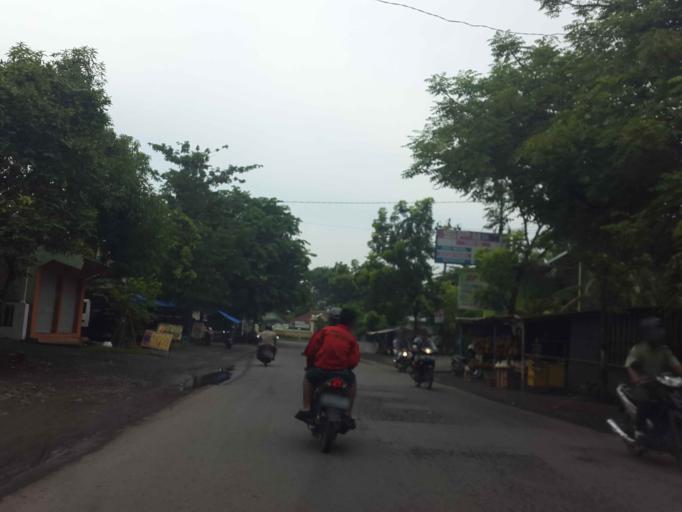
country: ID
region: Central Java
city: Mranggen
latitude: -6.9819
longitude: 110.4790
